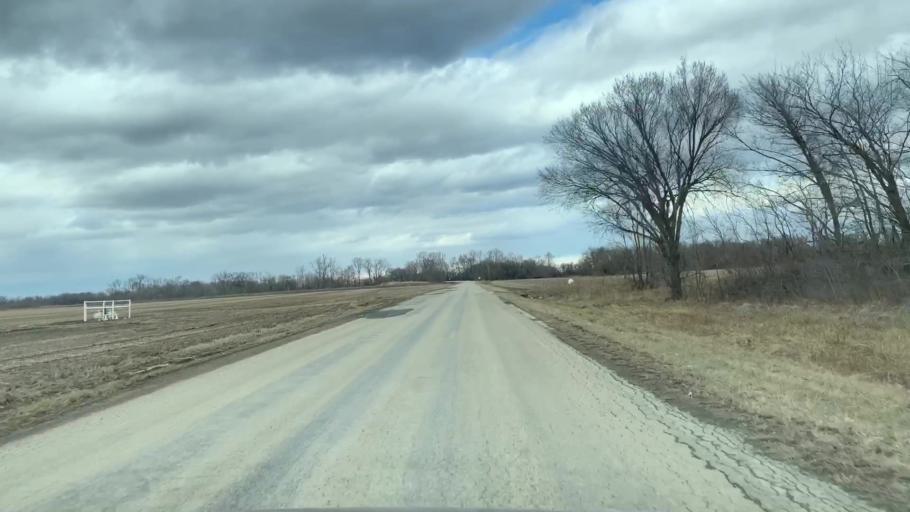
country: US
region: Kansas
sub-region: Allen County
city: Humboldt
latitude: 37.7978
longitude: -95.4706
